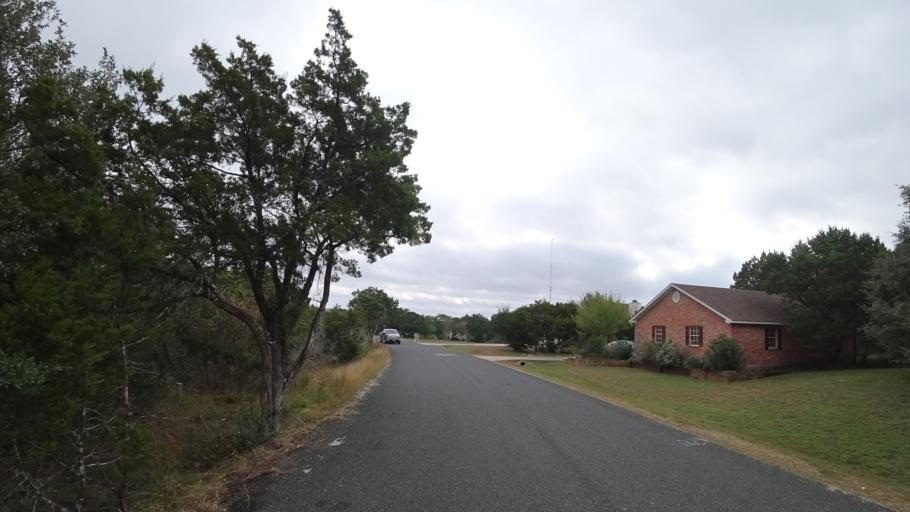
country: US
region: Texas
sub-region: Travis County
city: Barton Creek
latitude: 30.2540
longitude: -97.9070
